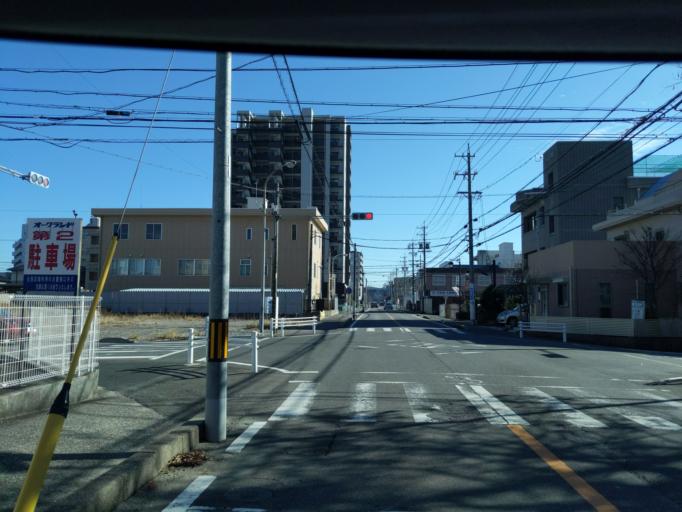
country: JP
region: Aichi
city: Kasugai
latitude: 35.2454
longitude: 136.9704
